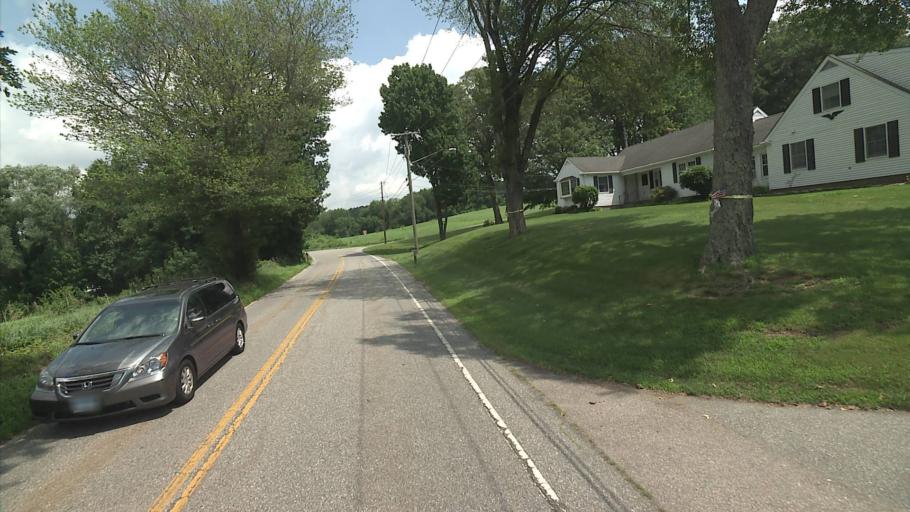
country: US
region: Connecticut
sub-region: New London County
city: Baltic
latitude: 41.6080
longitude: -72.1259
